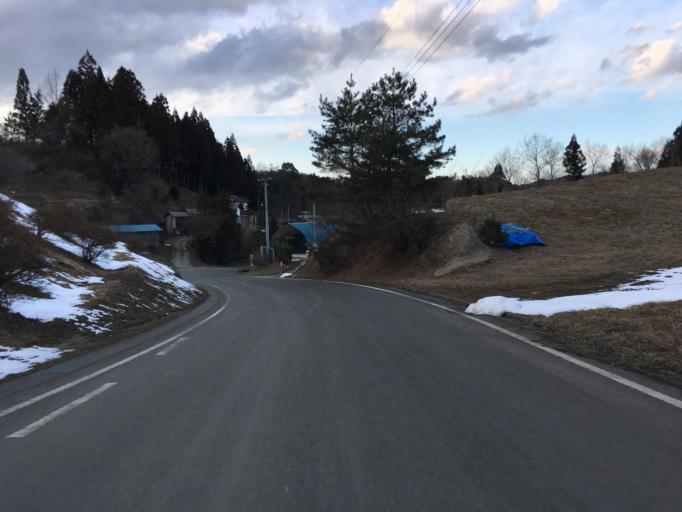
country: JP
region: Fukushima
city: Fukushima-shi
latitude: 37.6493
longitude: 140.5885
